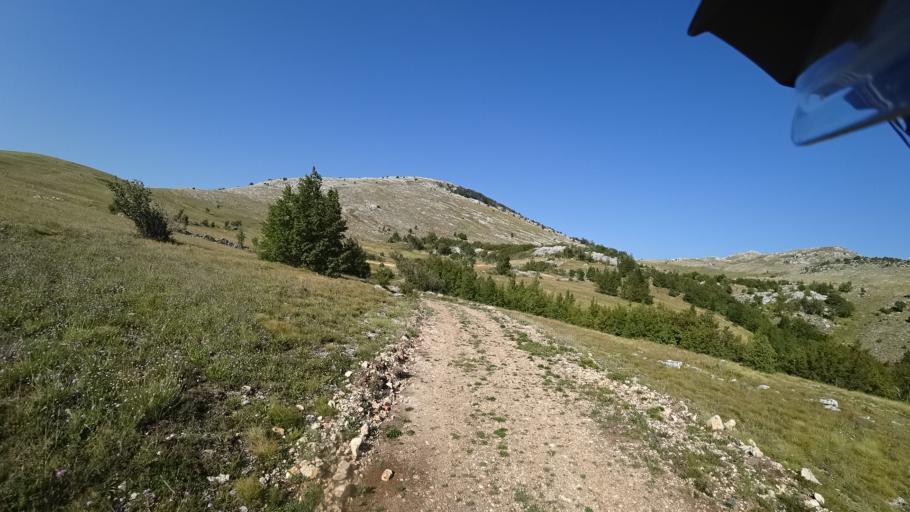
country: HR
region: Sibensko-Kniniska
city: Knin
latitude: 44.1993
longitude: 16.1629
